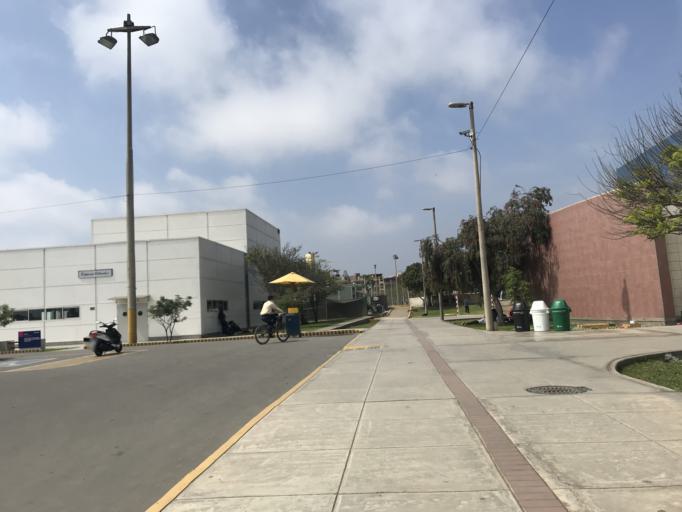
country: PE
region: Callao
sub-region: Callao
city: Callao
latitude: -12.0667
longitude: -77.0805
